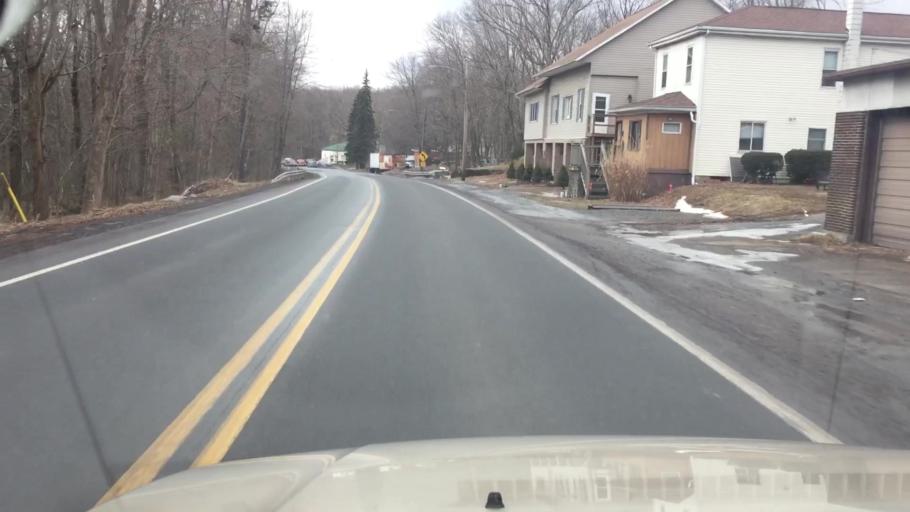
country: US
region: Pennsylvania
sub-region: Luzerne County
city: Harleigh
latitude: 40.9852
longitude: -75.9619
